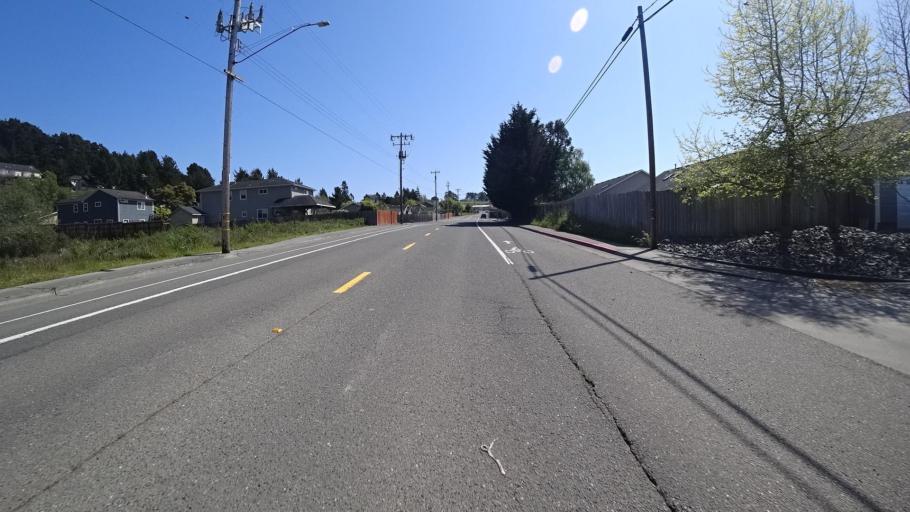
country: US
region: California
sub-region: Humboldt County
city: Hydesville
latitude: 40.5645
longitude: -124.1267
